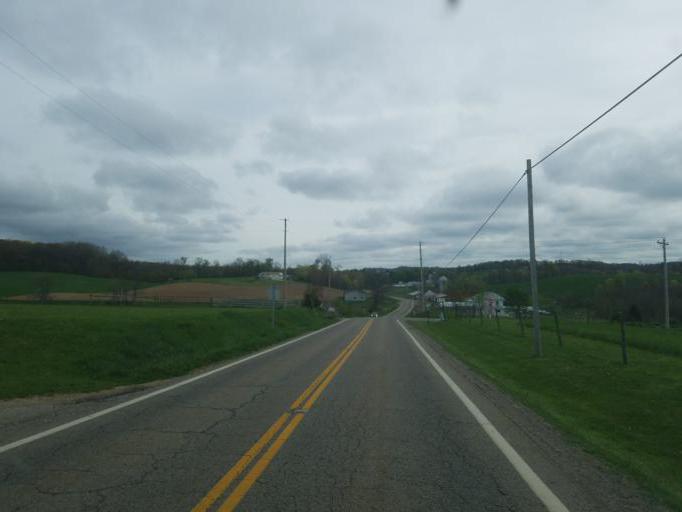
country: US
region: Ohio
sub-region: Ashland County
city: Loudonville
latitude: 40.5808
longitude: -82.1324
